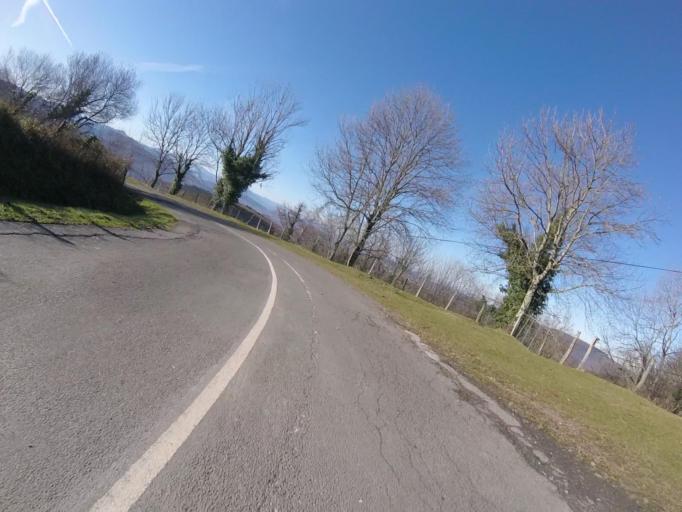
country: ES
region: Basque Country
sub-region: Provincia de Guipuzcoa
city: Irun
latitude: 43.2958
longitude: -1.8061
